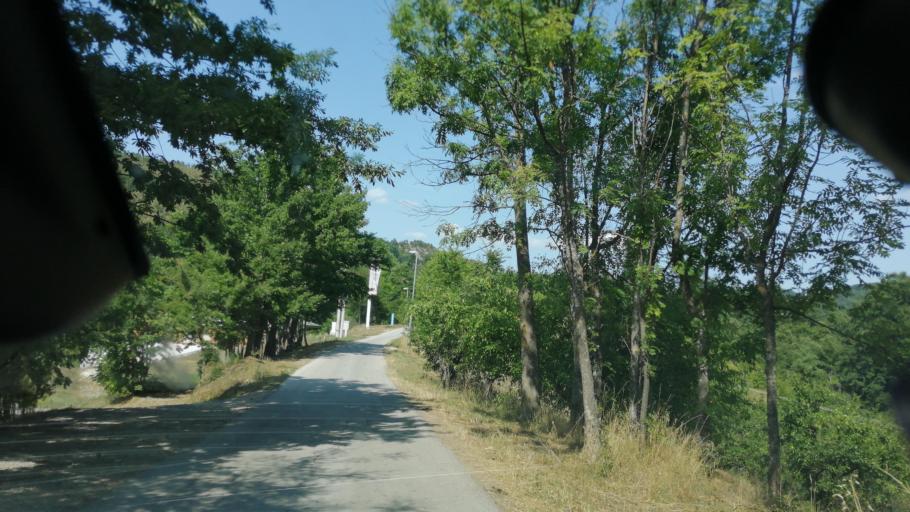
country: RS
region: Central Serbia
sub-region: Moravicki Okrug
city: Ivanjica
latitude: 43.6193
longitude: 20.2485
